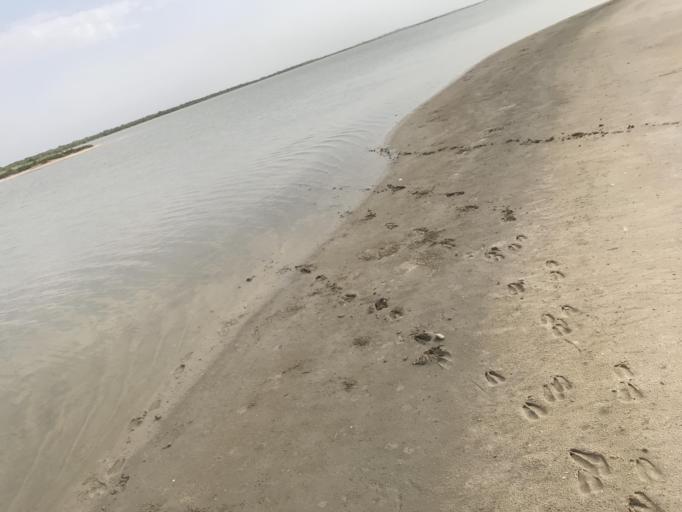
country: SN
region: Saint-Louis
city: Saint-Louis
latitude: 15.9276
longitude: -16.4635
